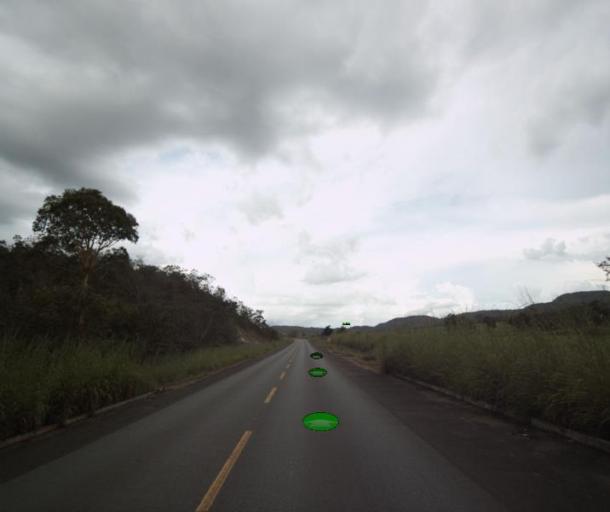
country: BR
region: Goias
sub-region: Niquelandia
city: Niquelandia
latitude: -14.5244
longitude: -48.5242
